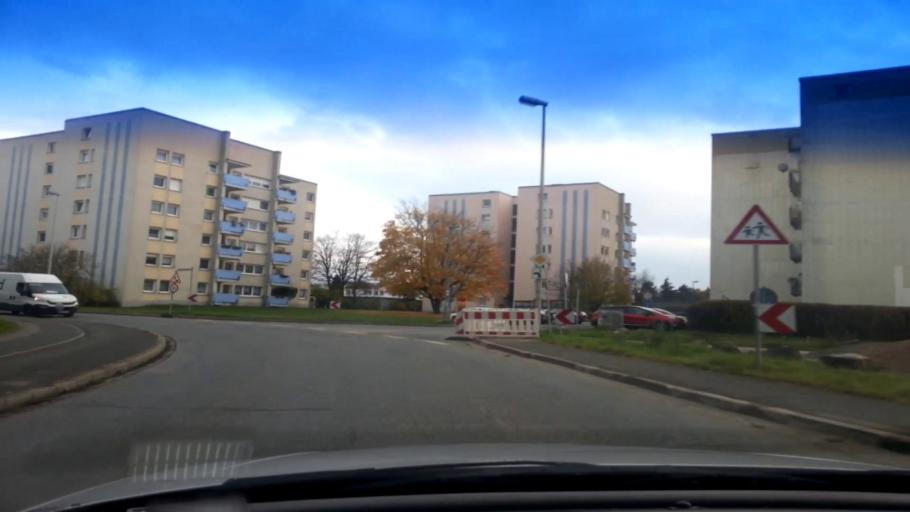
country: DE
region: Bavaria
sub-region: Upper Franconia
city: Gundelsheim
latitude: 49.9251
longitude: 10.9253
